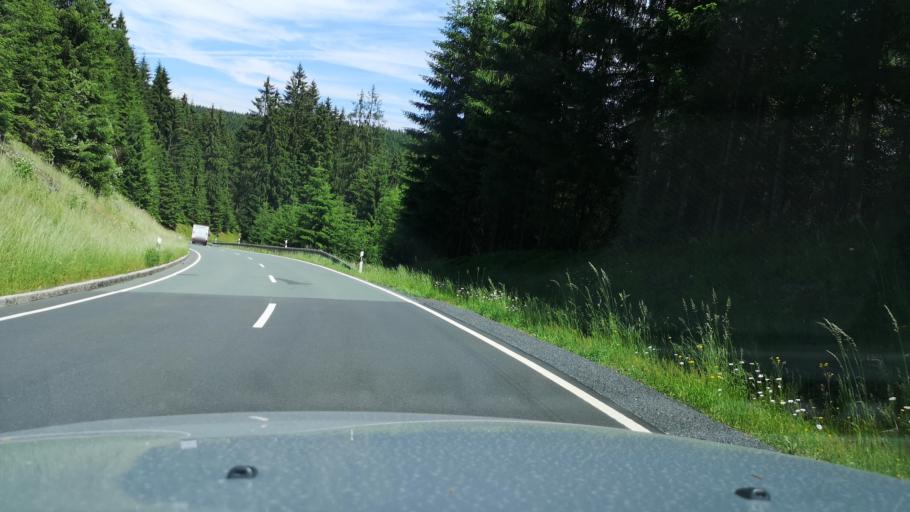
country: DE
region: Bavaria
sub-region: Upper Franconia
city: Tschirn
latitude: 50.3984
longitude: 11.4632
